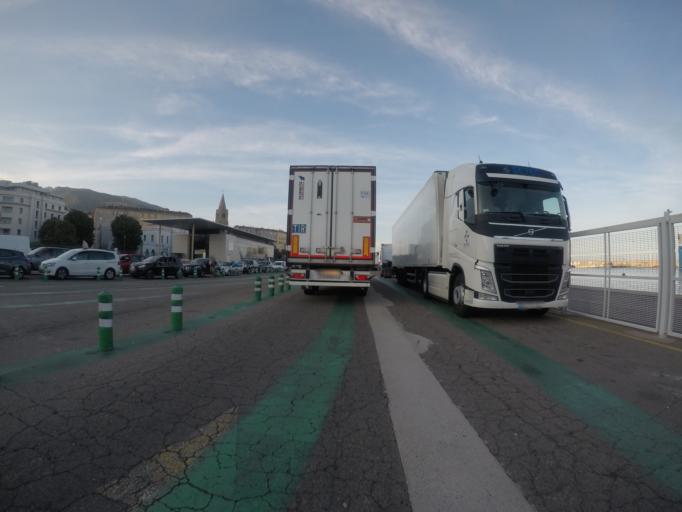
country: FR
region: Corsica
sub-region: Departement de la Haute-Corse
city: Bastia
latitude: 42.7014
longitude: 9.4532
